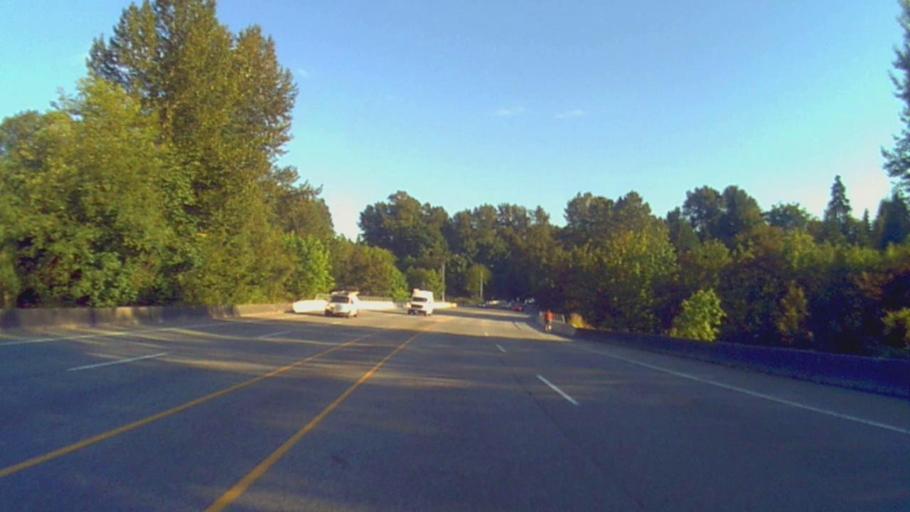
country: CA
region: British Columbia
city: New Westminster
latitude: 49.2480
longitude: -122.9129
